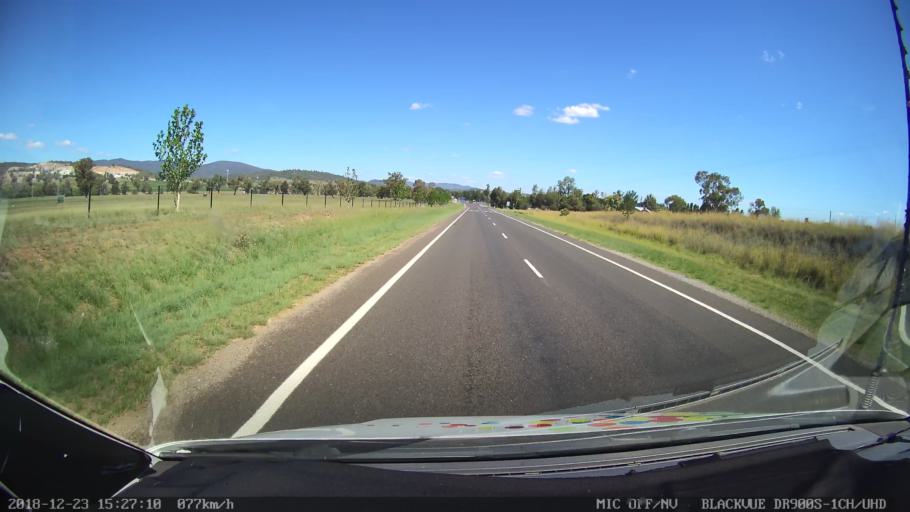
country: AU
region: New South Wales
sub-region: Tamworth Municipality
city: East Tamworth
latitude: -30.9251
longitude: 150.8437
